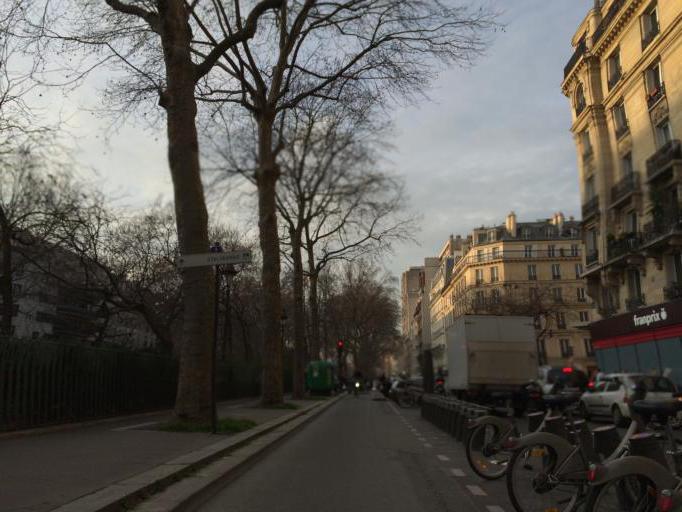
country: FR
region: Ile-de-France
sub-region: Paris
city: Paris
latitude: 48.8682
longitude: 2.3681
